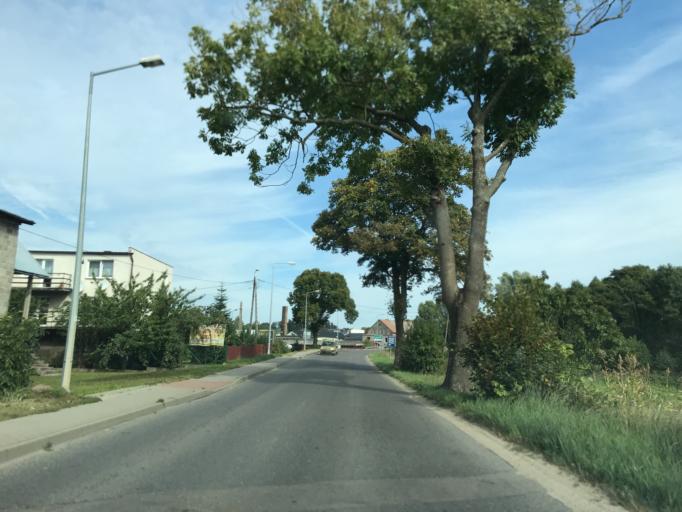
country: PL
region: Pomeranian Voivodeship
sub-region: Powiat pucki
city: Krokowa
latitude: 54.7804
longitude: 18.1683
